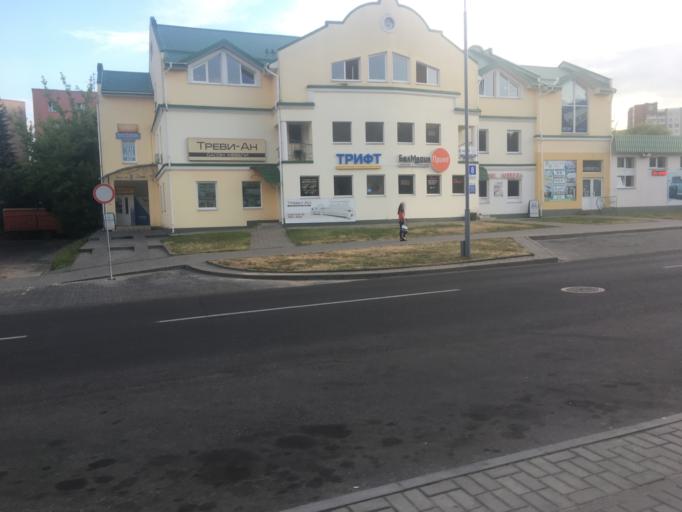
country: BY
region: Grodnenskaya
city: Hrodna
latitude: 53.6934
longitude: 23.8280
